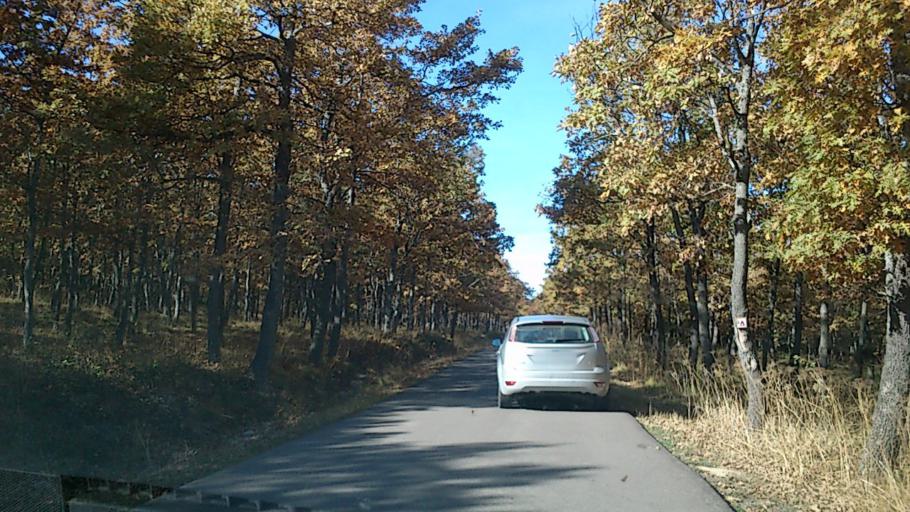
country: ES
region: Aragon
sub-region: Provincia de Zaragoza
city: Lituenigo
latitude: 41.8096
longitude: -1.8039
